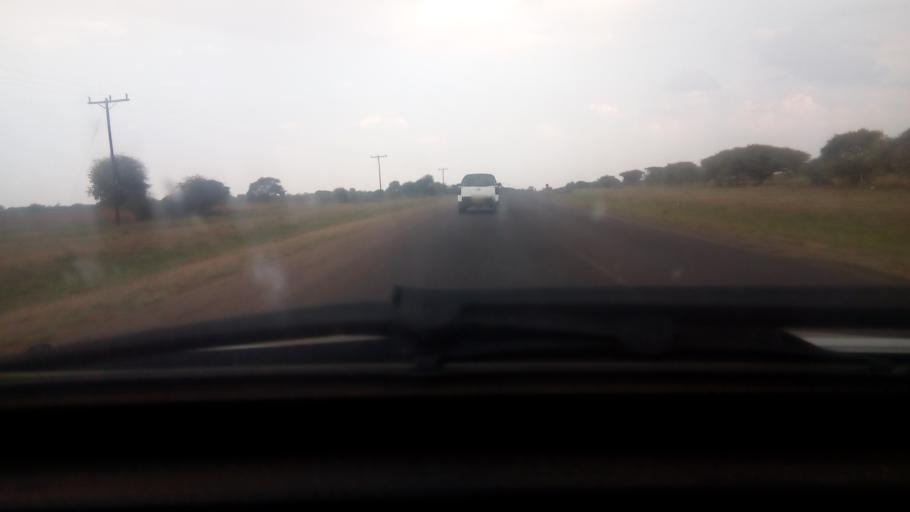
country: BW
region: Kweneng
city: Metsemotlhaba
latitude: -24.4793
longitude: 25.7295
